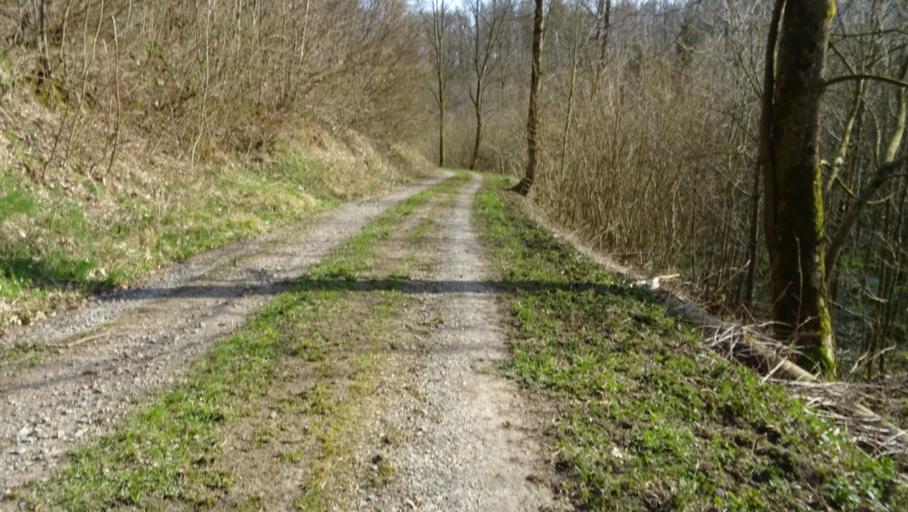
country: DE
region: Baden-Wuerttemberg
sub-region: Regierungsbezirk Stuttgart
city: Roigheim
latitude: 49.3808
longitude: 9.3478
